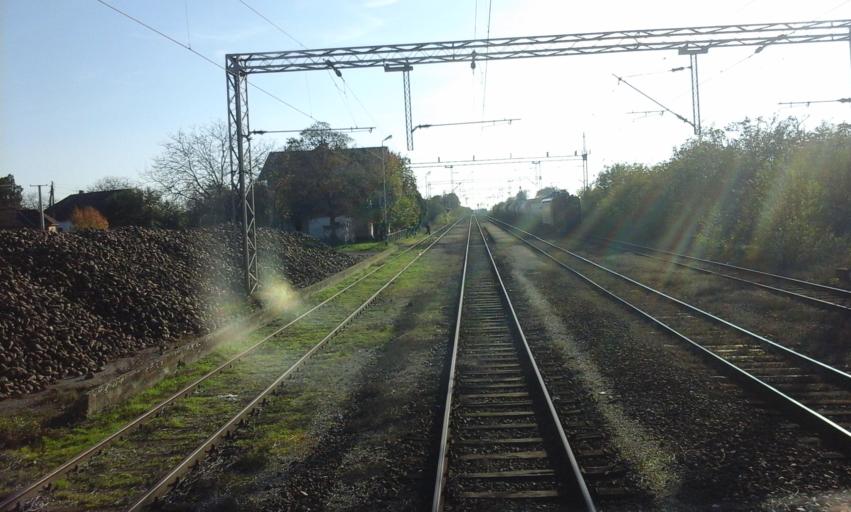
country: RS
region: Autonomna Pokrajina Vojvodina
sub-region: Severnobacki Okrug
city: Mali Igos
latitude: 45.6746
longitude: 19.6494
